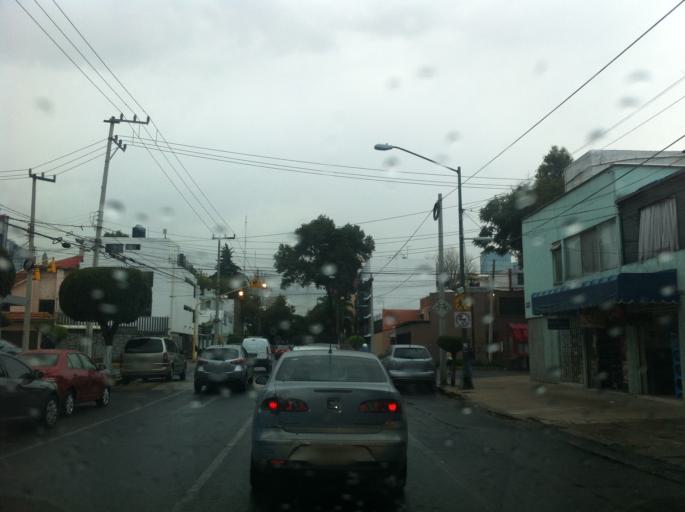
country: MX
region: Mexico City
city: Coyoacan
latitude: 19.3653
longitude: -99.1739
